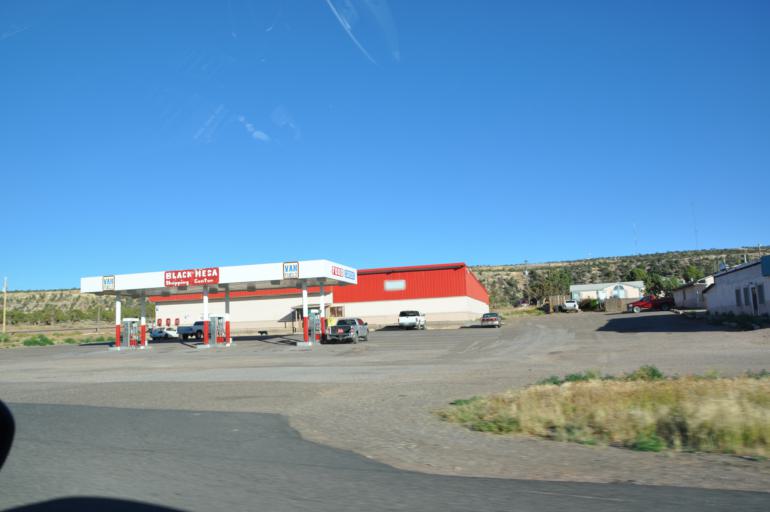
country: US
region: Arizona
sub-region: Navajo County
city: Kayenta
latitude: 36.5606
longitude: -110.5039
